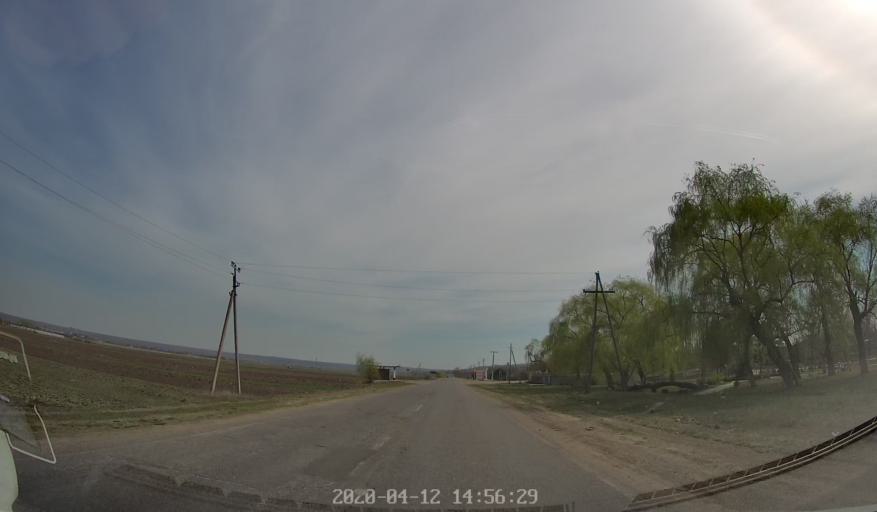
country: MD
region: Telenesti
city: Dubasari
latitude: 47.2616
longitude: 29.1297
